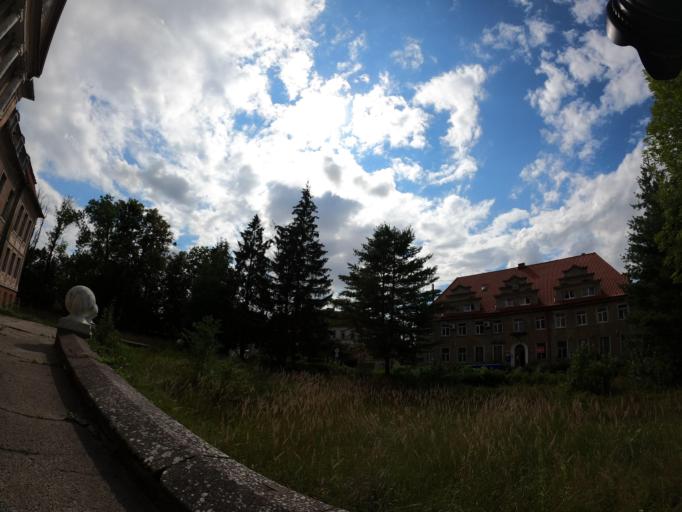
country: RU
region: Kaliningrad
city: Zheleznodorozhnyy
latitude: 54.3543
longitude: 21.3090
